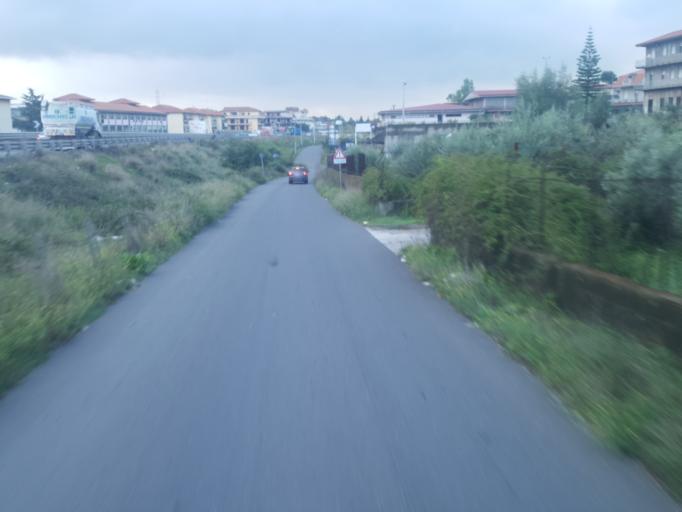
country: IT
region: Sicily
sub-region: Catania
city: Belvedere-Piano Tavola
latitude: 37.5338
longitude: 14.9861
